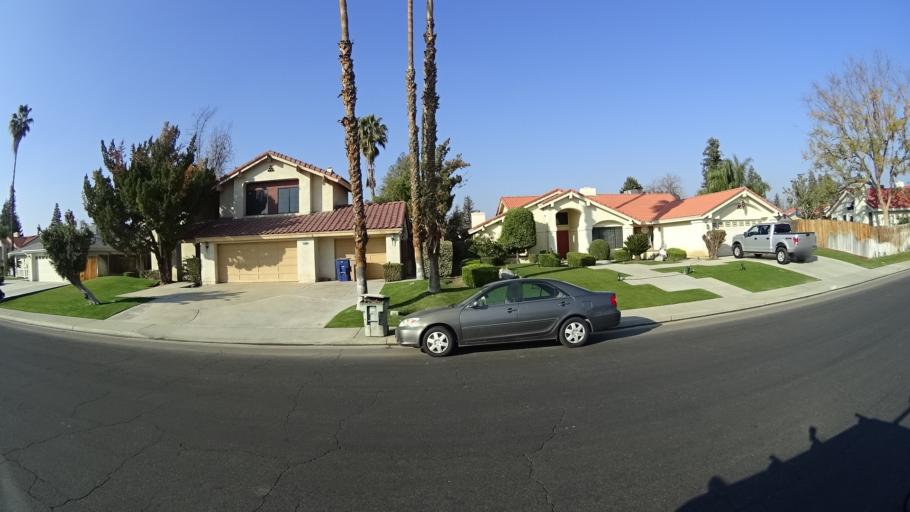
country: US
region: California
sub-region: Kern County
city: Greenacres
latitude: 35.3357
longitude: -119.1100
